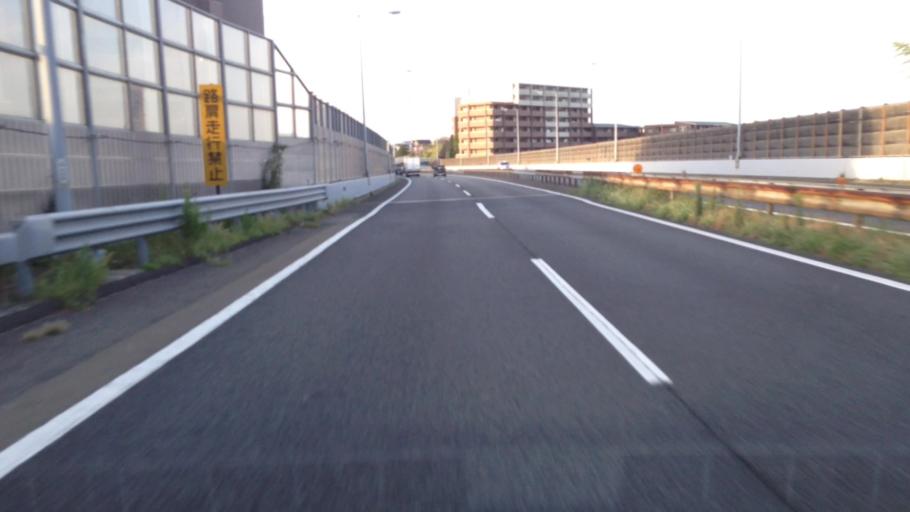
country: JP
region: Kanagawa
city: Yokohama
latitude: 35.3976
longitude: 139.5749
